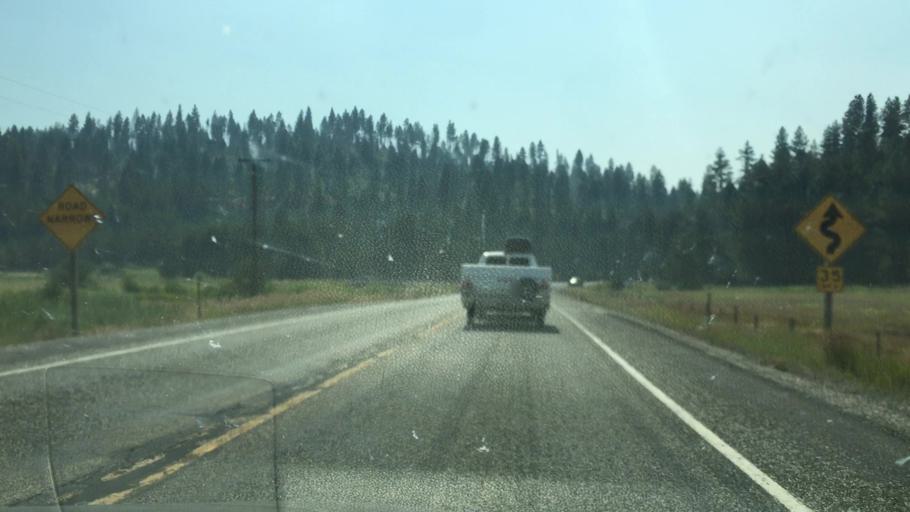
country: US
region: Idaho
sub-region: Valley County
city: Cascade
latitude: 44.3362
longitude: -116.0339
